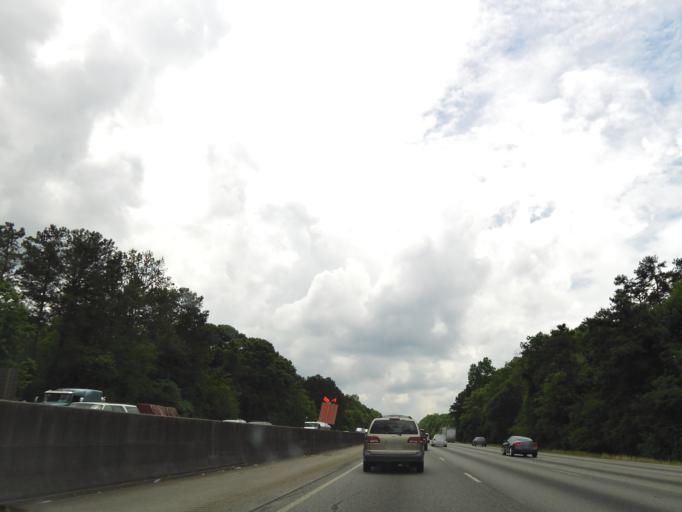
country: US
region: Georgia
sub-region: Cobb County
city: Mableton
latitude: 33.7744
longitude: -84.5680
